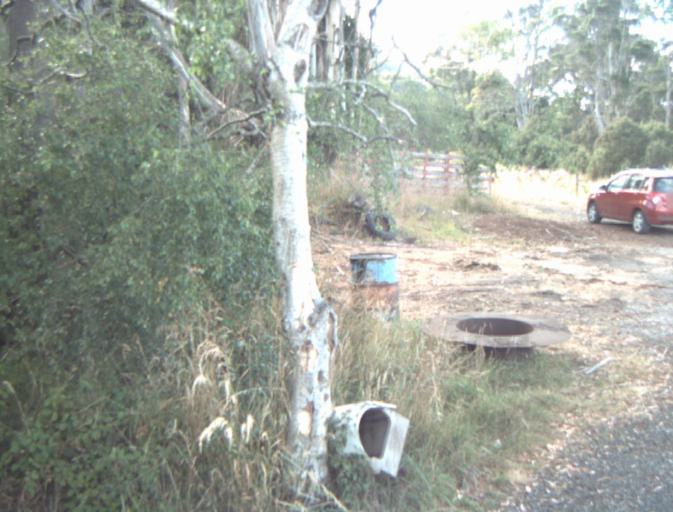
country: AU
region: Tasmania
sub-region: Launceston
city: Mayfield
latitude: -41.2708
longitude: 147.1750
